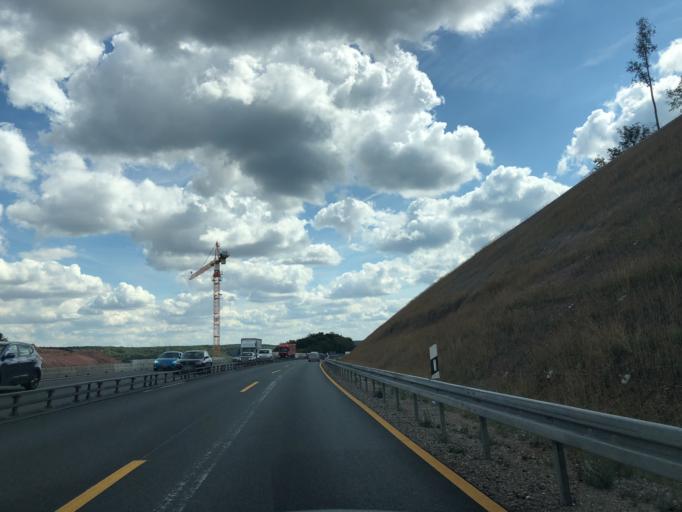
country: DE
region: Bavaria
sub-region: Regierungsbezirk Unterfranken
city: Altenbuch
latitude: 49.8897
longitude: 9.4121
